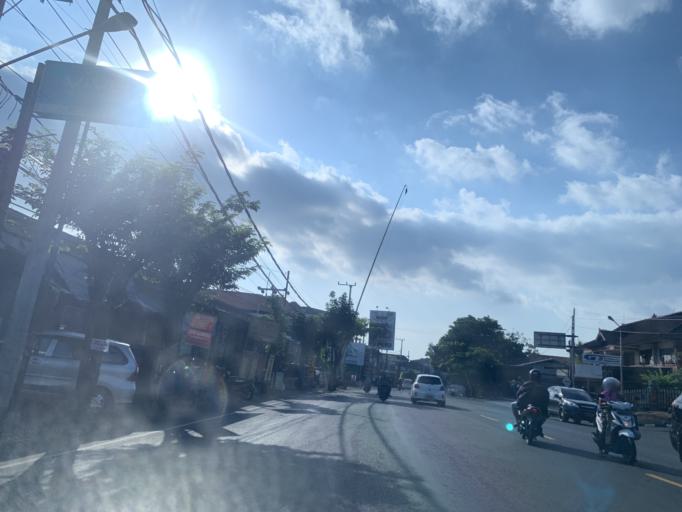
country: ID
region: Bali
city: Banjar Bongangede
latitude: -8.5499
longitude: 115.1232
